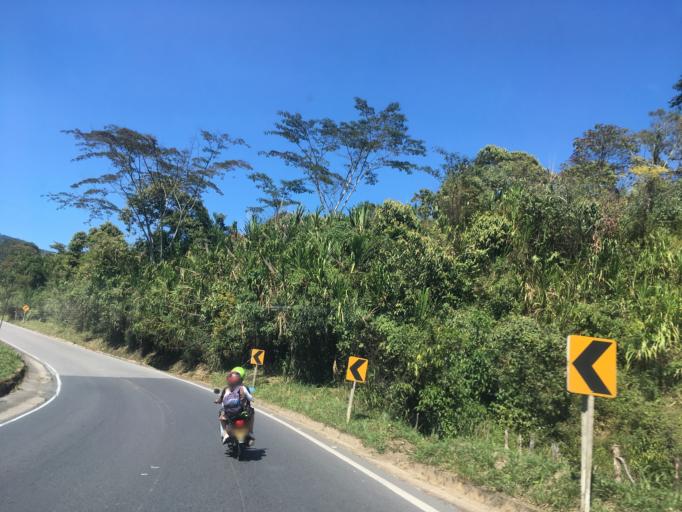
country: CO
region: Santander
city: Suaita
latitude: 6.0852
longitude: -73.3864
